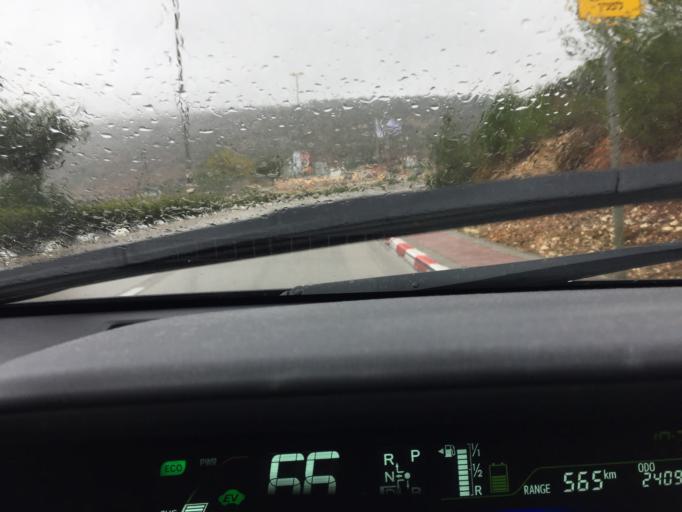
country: PS
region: West Bank
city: Kifil Haris
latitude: 32.1016
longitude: 35.1646
